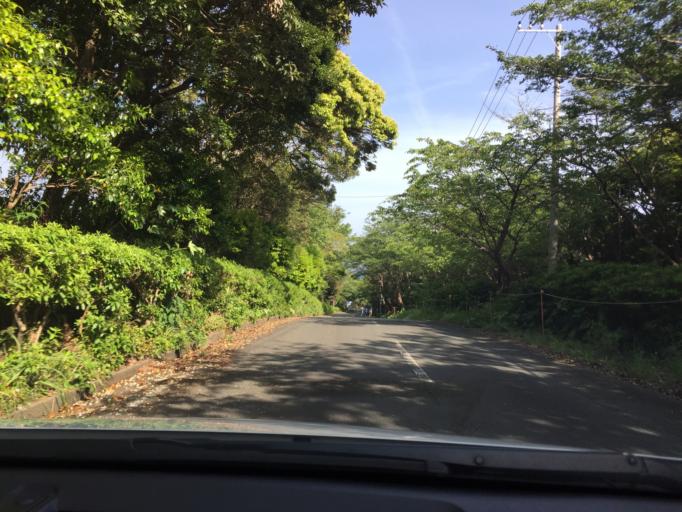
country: JP
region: Shizuoka
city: Shimoda
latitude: 34.6640
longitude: 138.9811
